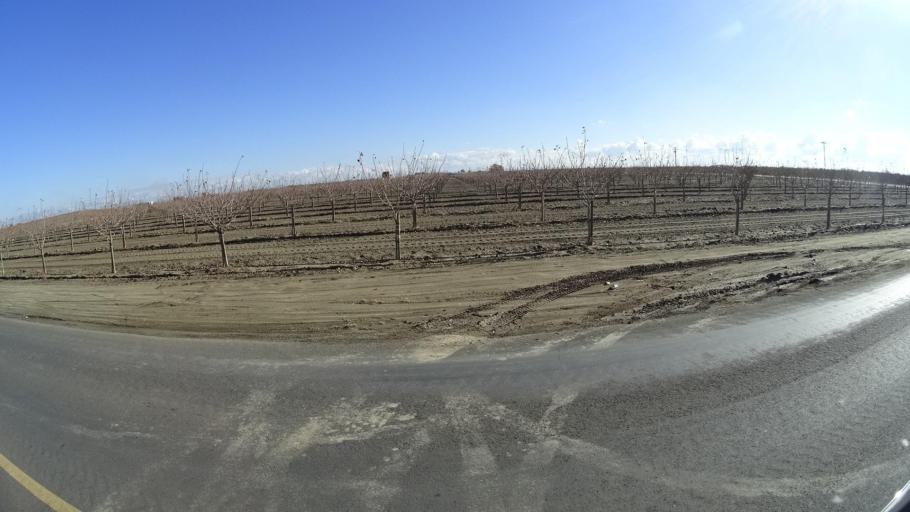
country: US
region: California
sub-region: Kern County
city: Delano
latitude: 35.7333
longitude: -119.2584
